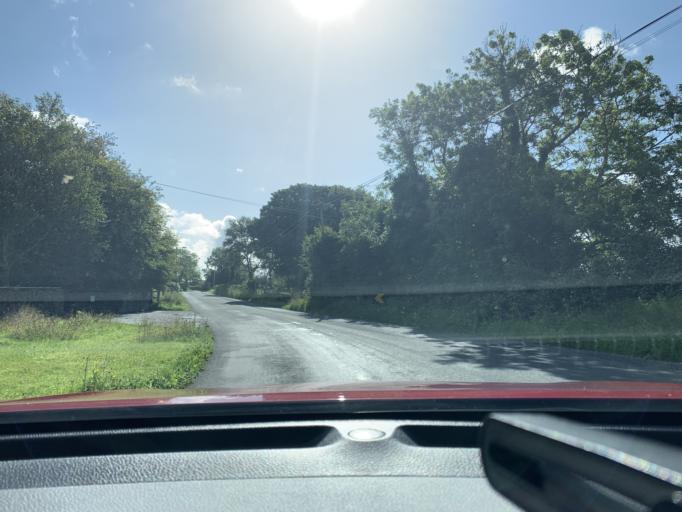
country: IE
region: Connaught
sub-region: Sligo
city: Strandhill
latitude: 54.3391
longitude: -8.5420
